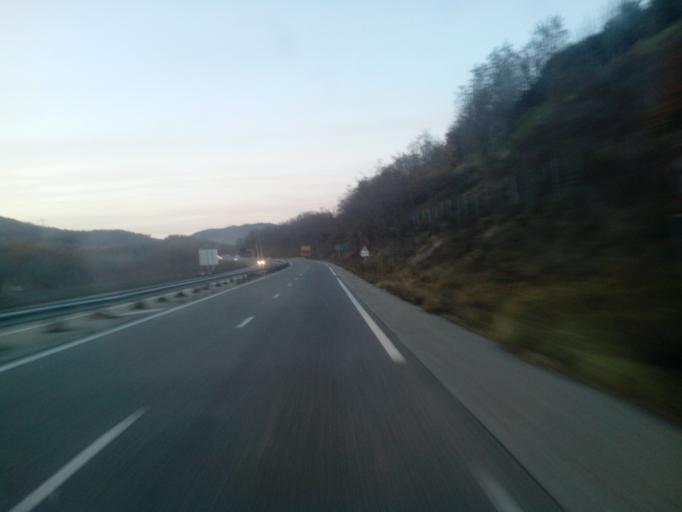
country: FR
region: Midi-Pyrenees
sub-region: Departement de l'Ariege
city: Montgaillard
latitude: 42.9267
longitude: 1.6334
